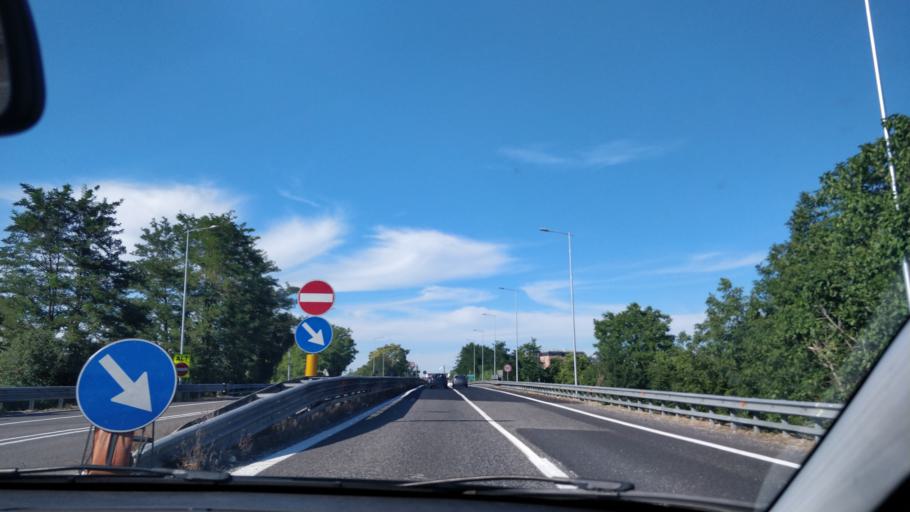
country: IT
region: Abruzzo
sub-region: Provincia di Chieti
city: Casalincontrada
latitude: 42.3390
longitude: 14.1296
